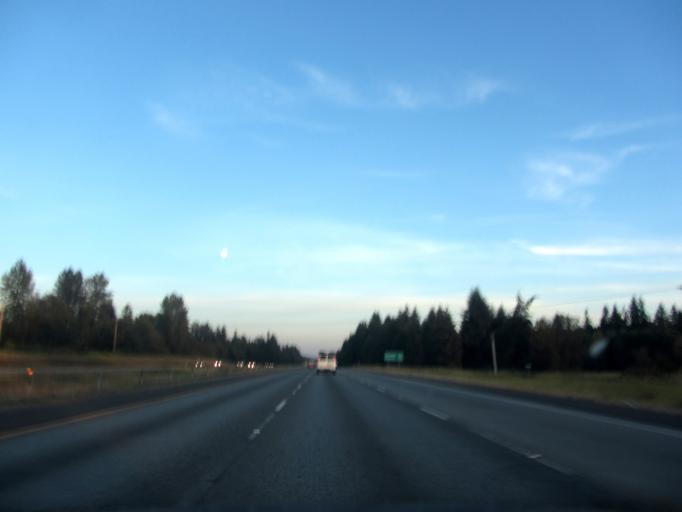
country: US
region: Washington
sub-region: Snohomish County
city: Stanwood
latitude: 48.2910
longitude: -122.2963
